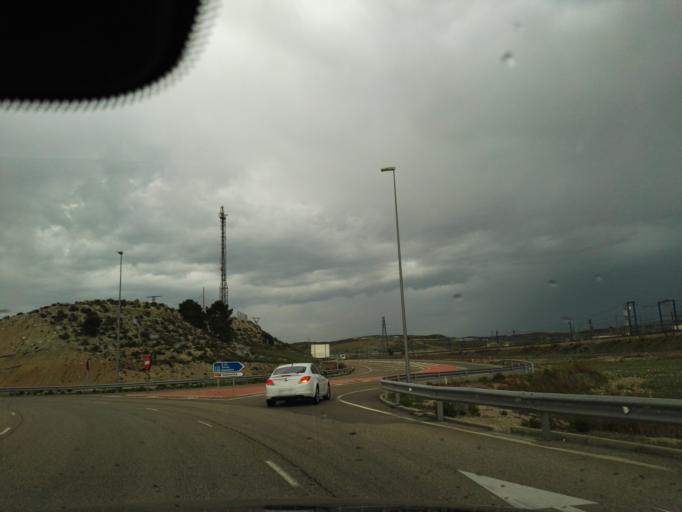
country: ES
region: Aragon
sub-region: Provincia de Zaragoza
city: Montecanal
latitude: 41.6274
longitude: -0.9902
